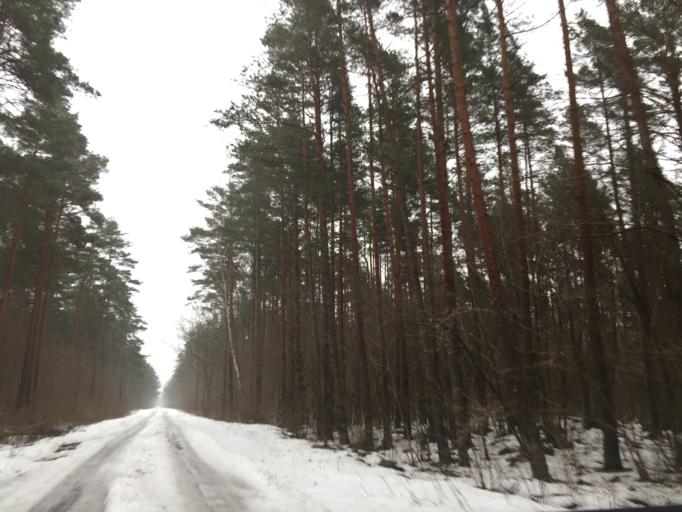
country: EE
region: Saare
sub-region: Kuressaare linn
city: Kuressaare
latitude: 58.2698
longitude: 22.5499
